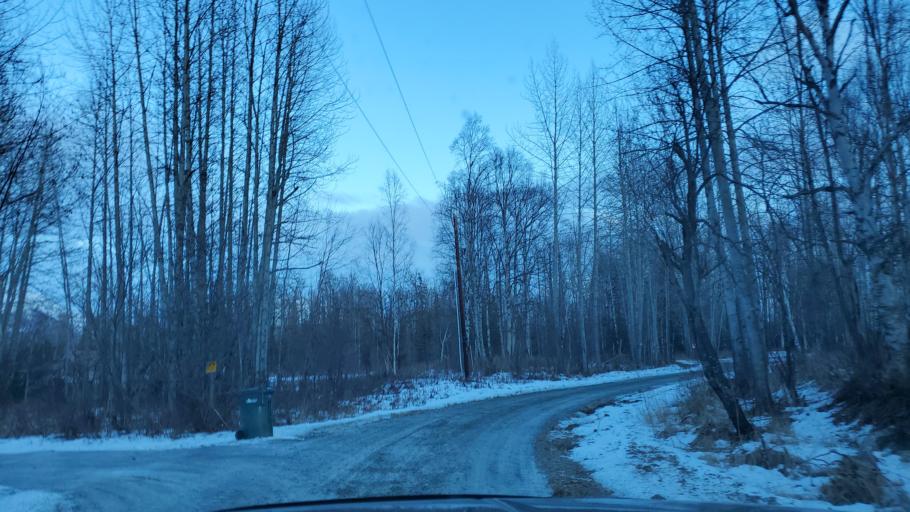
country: US
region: Alaska
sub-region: Matanuska-Susitna Borough
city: Lakes
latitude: 61.6669
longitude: -149.3322
